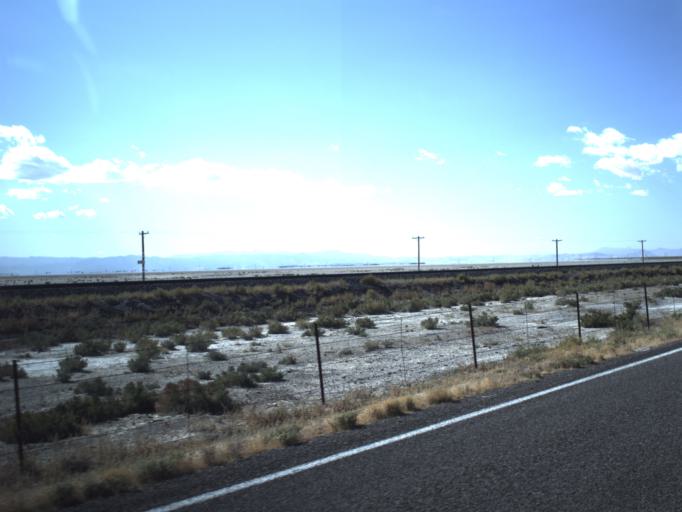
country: US
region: Utah
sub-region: Millard County
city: Delta
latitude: 39.1857
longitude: -112.6970
